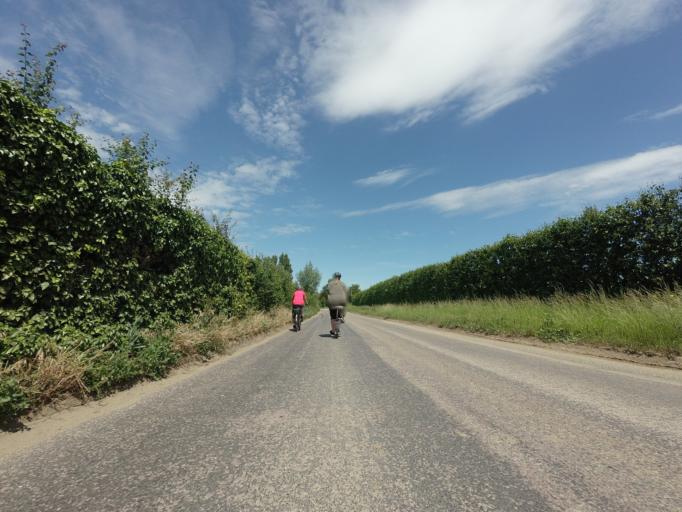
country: GB
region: England
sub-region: Kent
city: Cliffe
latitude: 51.4483
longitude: 0.4906
